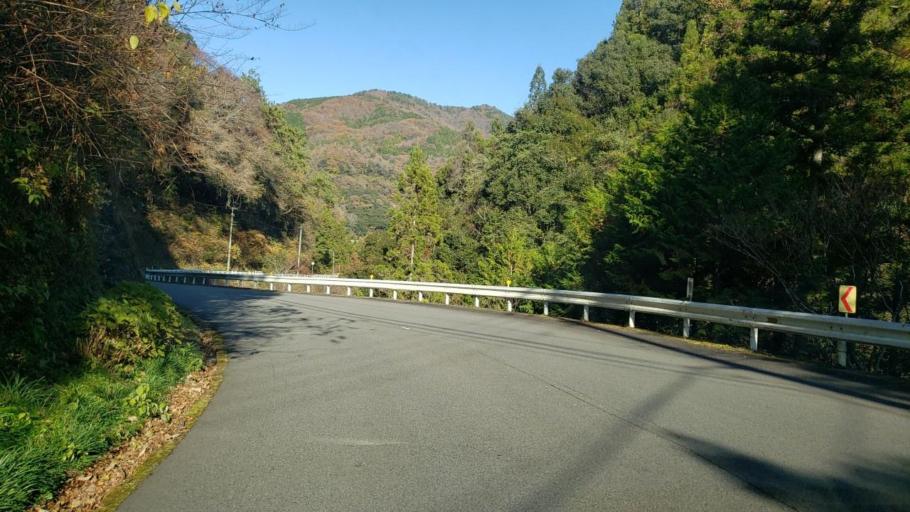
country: JP
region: Tokushima
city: Wakimachi
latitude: 34.0169
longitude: 134.0349
